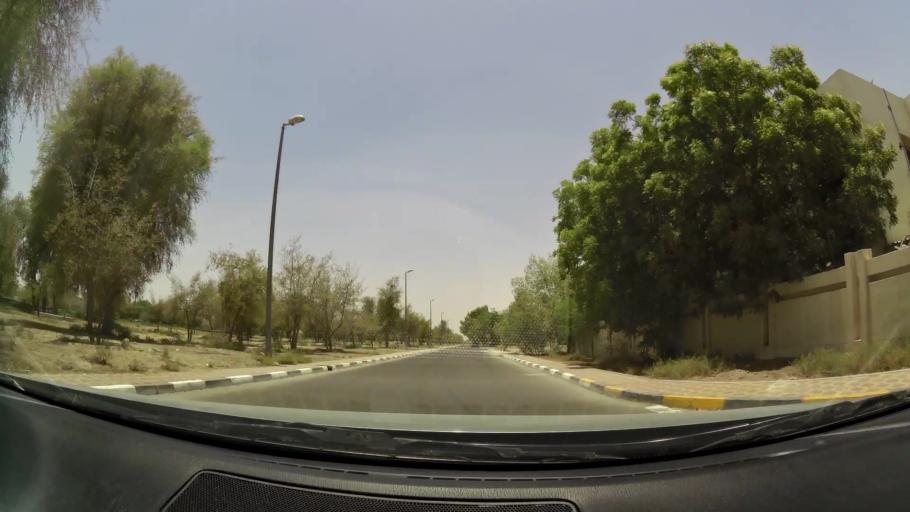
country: OM
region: Al Buraimi
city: Al Buraymi
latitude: 24.2595
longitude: 55.7279
